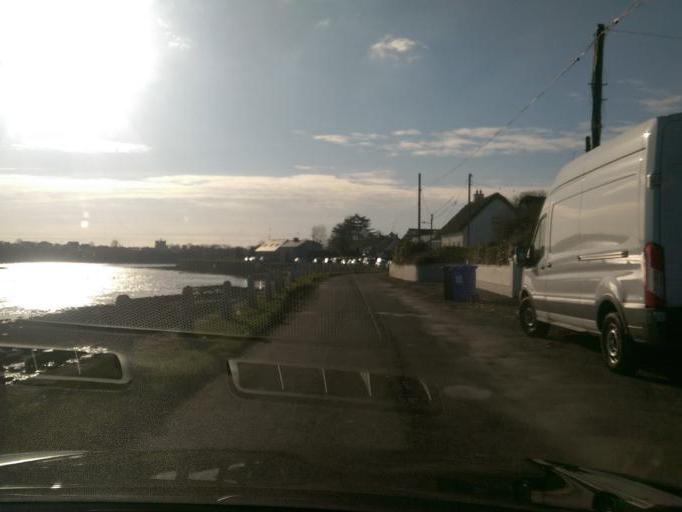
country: IE
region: Connaught
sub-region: County Galway
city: Oranmore
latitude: 53.2110
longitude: -8.8925
